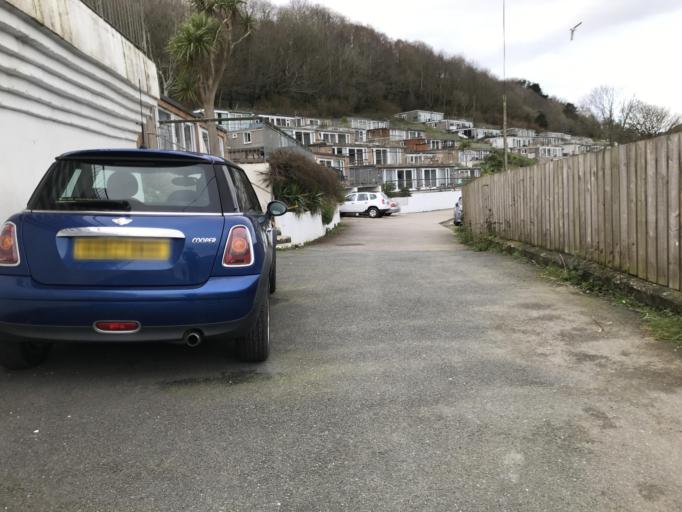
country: GB
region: England
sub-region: Cornwall
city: Looe
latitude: 50.3617
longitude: -4.4370
